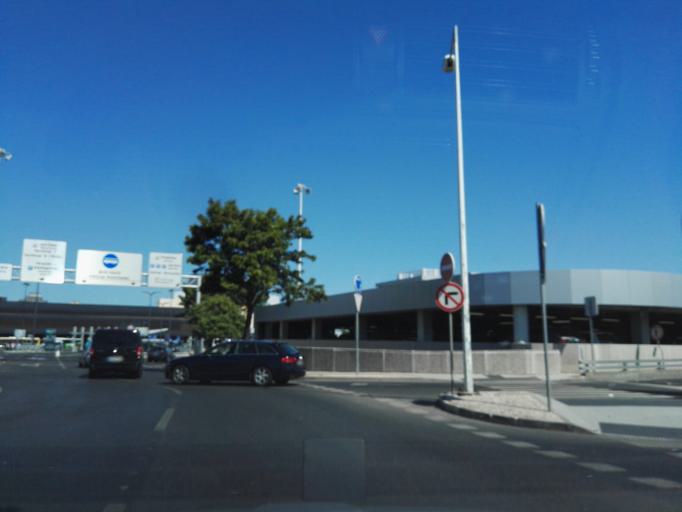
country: PT
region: Lisbon
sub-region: Loures
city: Moscavide
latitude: 38.7670
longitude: -9.1289
